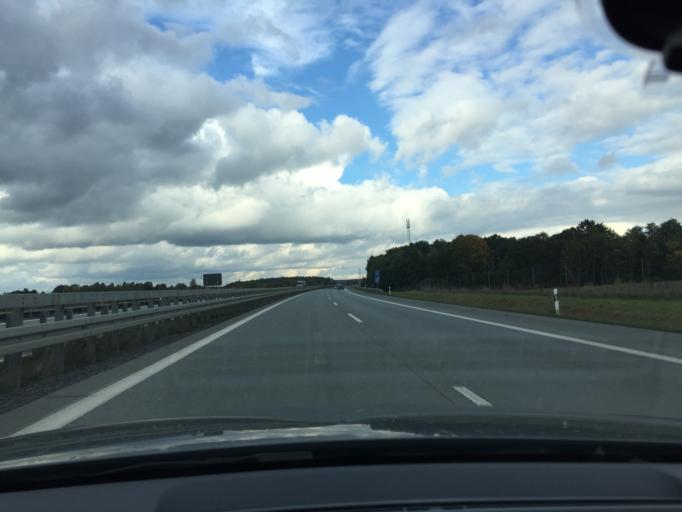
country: DE
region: Saxony
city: Schonfeld
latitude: 51.3270
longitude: 13.7186
